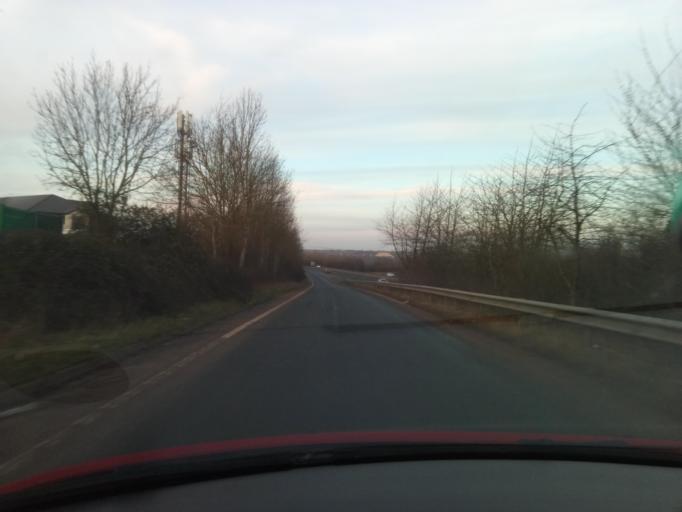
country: GB
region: England
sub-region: Leicestershire
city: Mountsorrel
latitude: 52.7201
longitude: -1.1282
